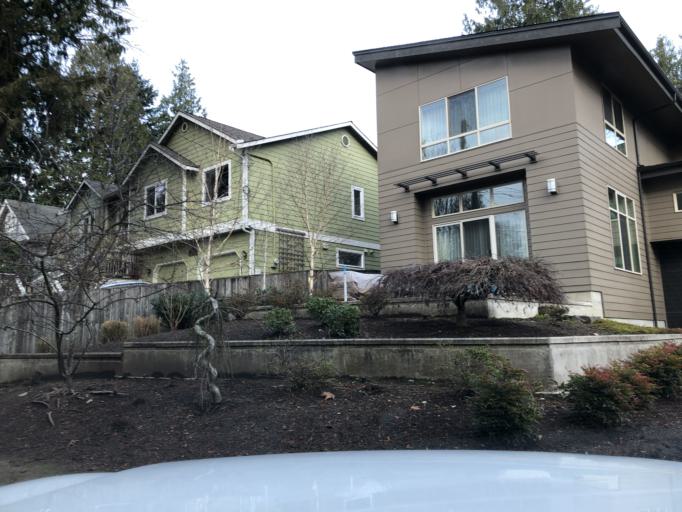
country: US
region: Washington
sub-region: King County
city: Inglewood-Finn Hill
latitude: 47.7060
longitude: -122.2802
